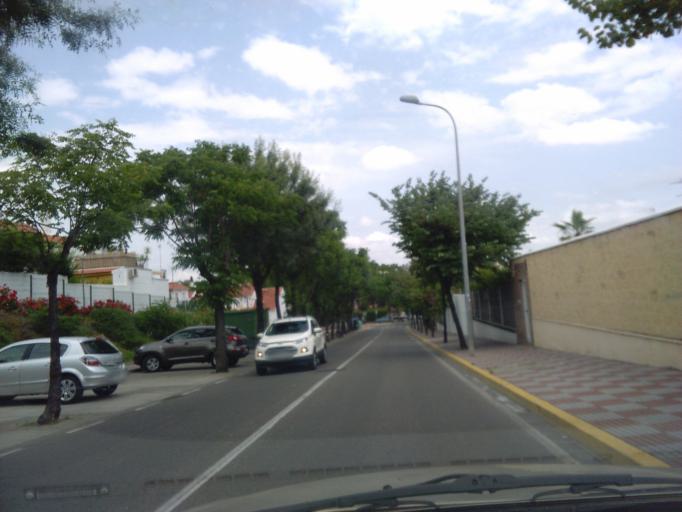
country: ES
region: Andalusia
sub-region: Provincia de Sevilla
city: Tomares
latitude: 37.3703
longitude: -6.0406
